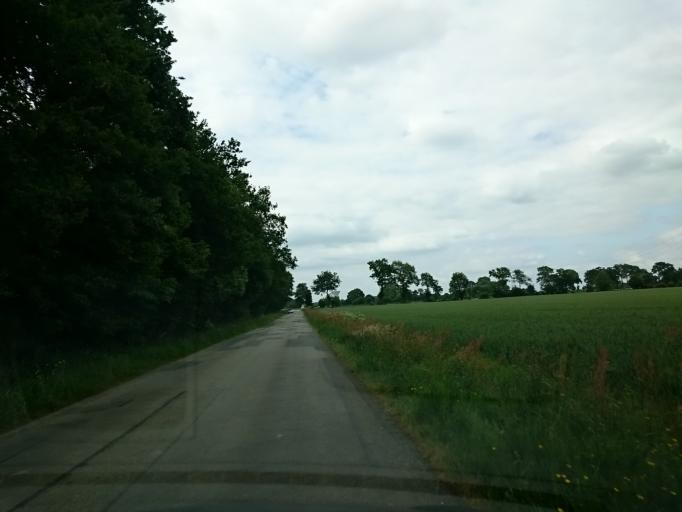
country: FR
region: Brittany
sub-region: Departement d'Ille-et-Vilaine
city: Crevin
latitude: 47.9346
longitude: -1.6330
